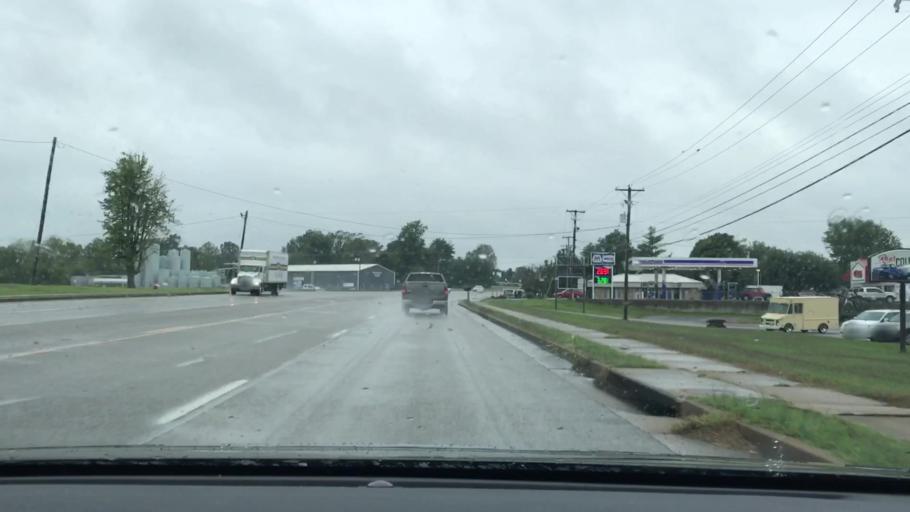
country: US
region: Kentucky
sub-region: Hopkins County
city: Madisonville
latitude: 37.3259
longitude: -87.4558
